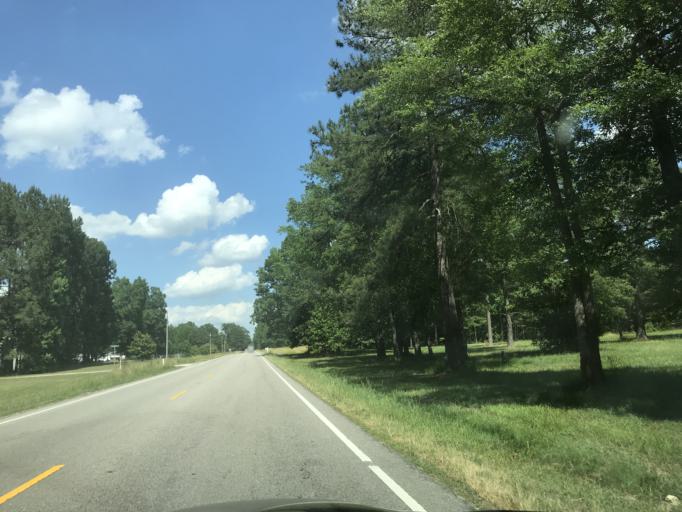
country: US
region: North Carolina
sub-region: Wake County
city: Rolesville
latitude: 35.9718
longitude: -78.3834
